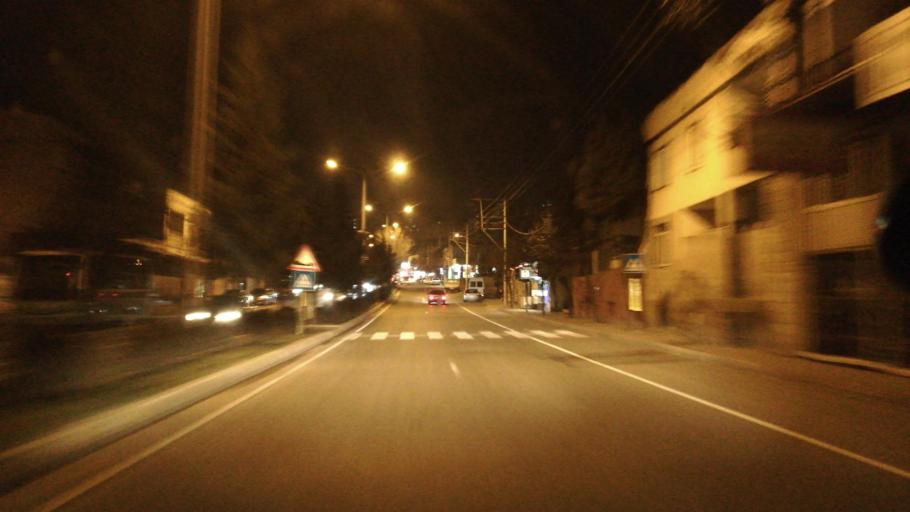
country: TR
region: Kahramanmaras
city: Kahramanmaras
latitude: 37.5947
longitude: 36.9085
